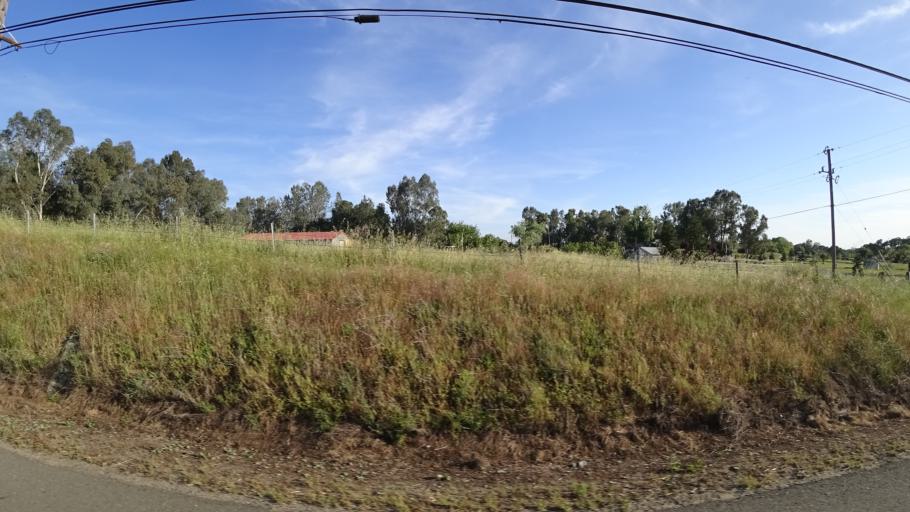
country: US
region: California
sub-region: Placer County
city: Lincoln
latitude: 38.9265
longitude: -121.2617
